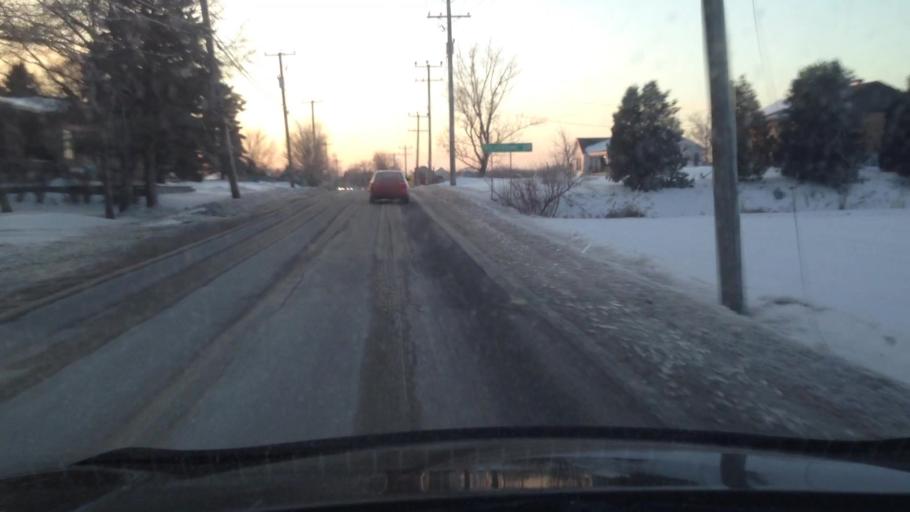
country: CA
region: Quebec
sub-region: Lanaudiere
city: Saint-Lin-Laurentides
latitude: 45.8520
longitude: -73.7665
